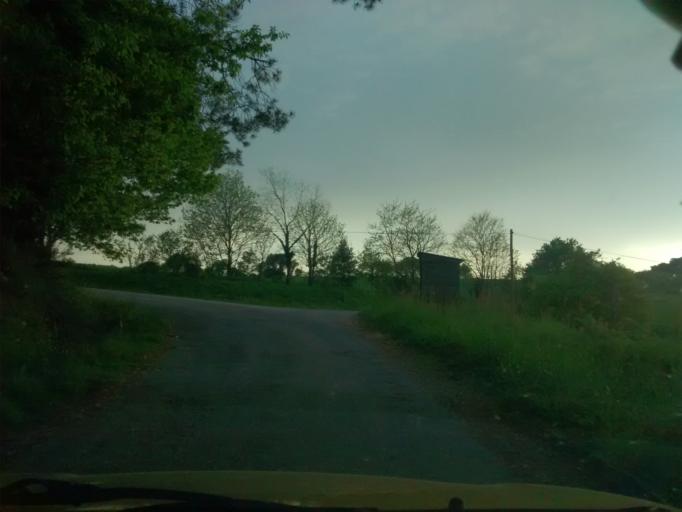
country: FR
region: Brittany
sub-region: Departement du Morbihan
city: Pleucadeuc
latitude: 47.7737
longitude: -2.4042
